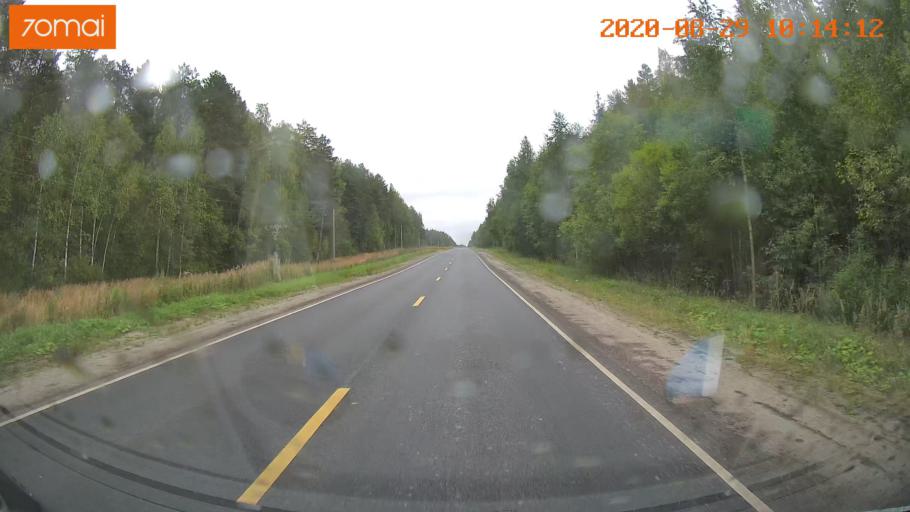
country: RU
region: Ivanovo
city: Yur'yevets
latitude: 57.3552
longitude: 42.7486
